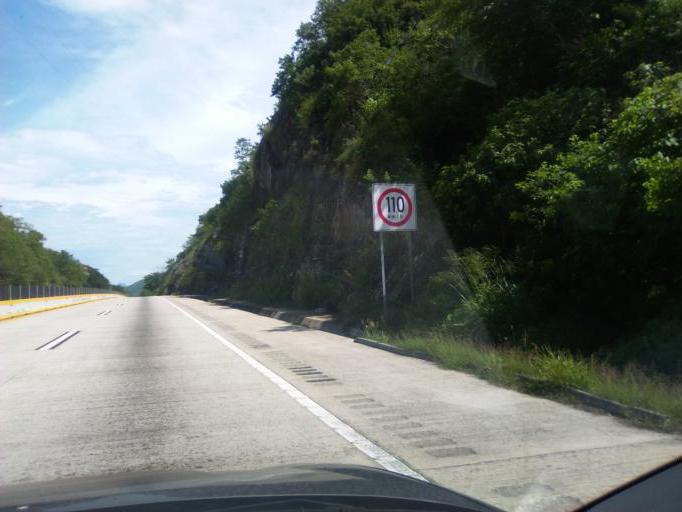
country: MX
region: Guerrero
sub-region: Acapulco de Juarez
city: Kilometro 30
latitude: 16.9997
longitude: -99.6890
